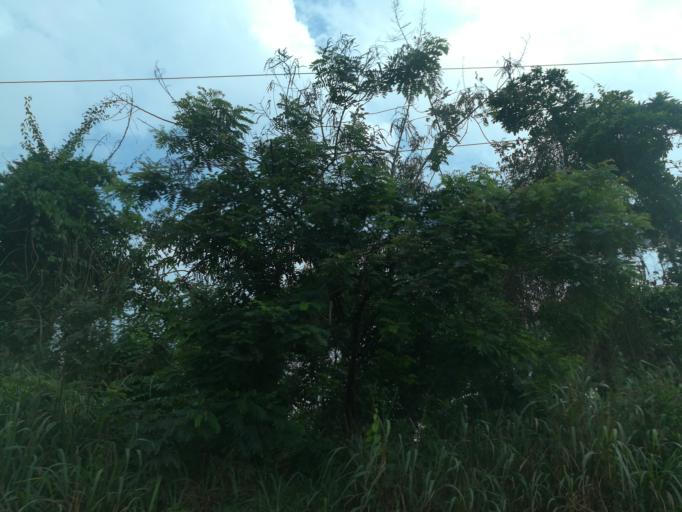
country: NG
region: Lagos
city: Ikorodu
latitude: 6.6641
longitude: 3.6023
